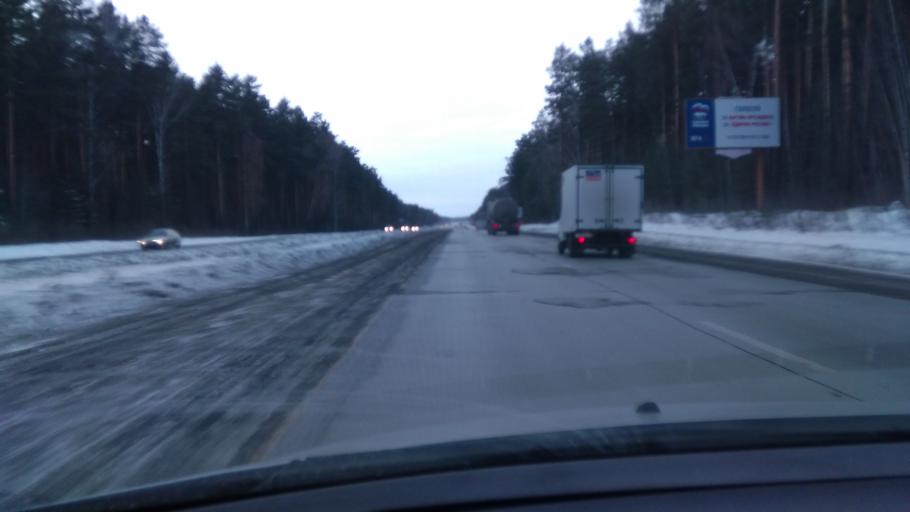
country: RU
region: Sverdlovsk
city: Sysert'
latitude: 56.5791
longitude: 60.8564
